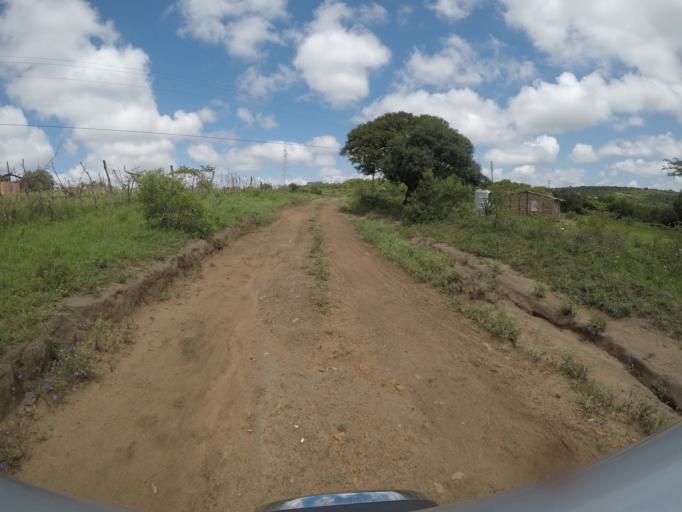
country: ZA
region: KwaZulu-Natal
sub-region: uThungulu District Municipality
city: Empangeni
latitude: -28.5832
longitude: 31.8349
